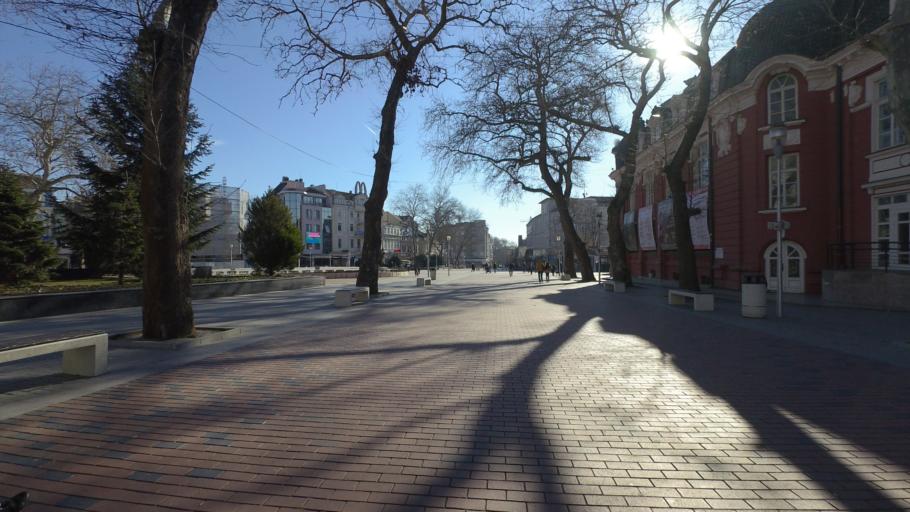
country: BG
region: Varna
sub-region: Obshtina Varna
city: Varna
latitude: 43.2039
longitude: 27.9118
